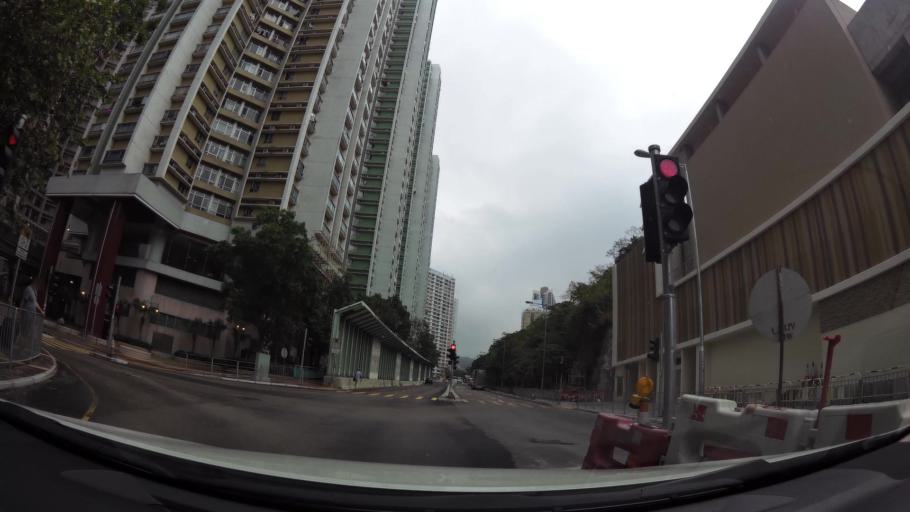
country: HK
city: Yung Shue Wan
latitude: 22.2420
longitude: 114.1493
